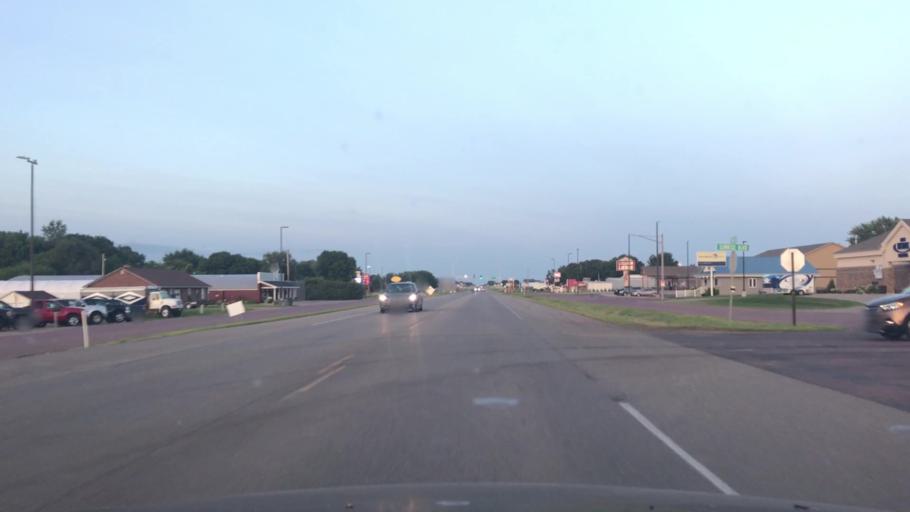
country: US
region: Minnesota
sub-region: Redwood County
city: Redwood Falls
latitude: 44.5414
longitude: -95.1051
